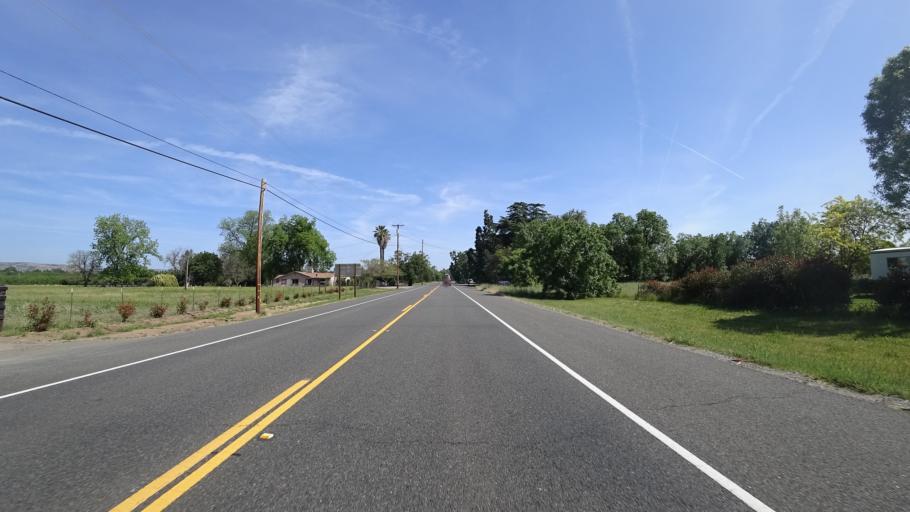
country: US
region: California
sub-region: Tehama County
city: Gerber
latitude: 40.1360
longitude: -122.1270
